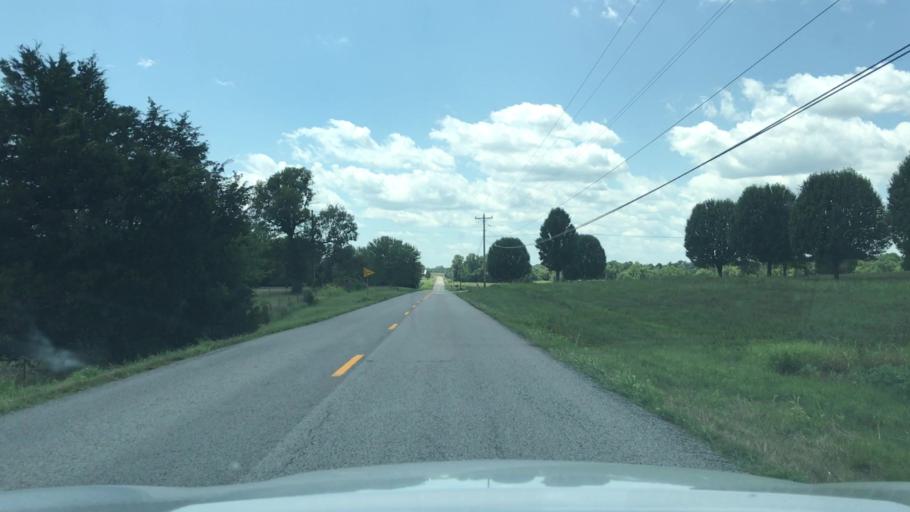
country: US
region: Kentucky
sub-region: Christian County
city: Hopkinsville
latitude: 36.9672
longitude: -87.3833
